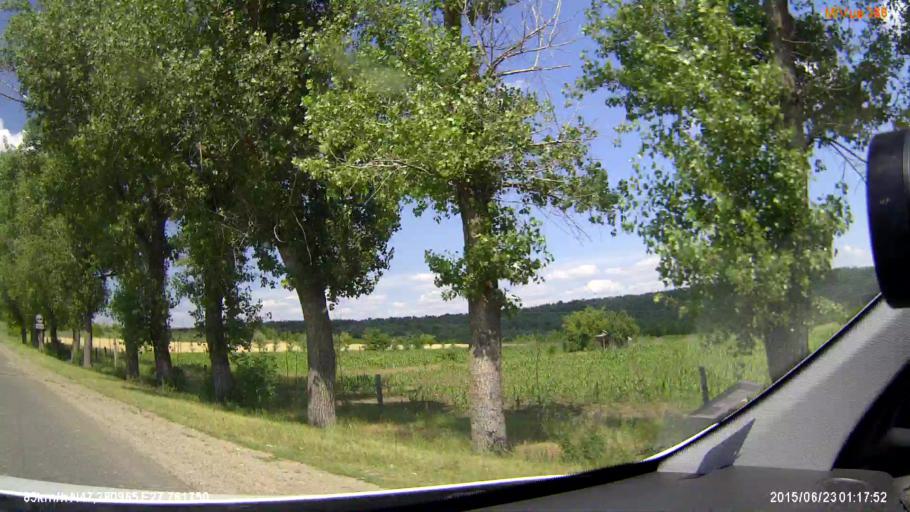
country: RO
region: Iasi
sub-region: Comuna Ungheni
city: Bosia
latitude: 47.2808
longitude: 27.7617
